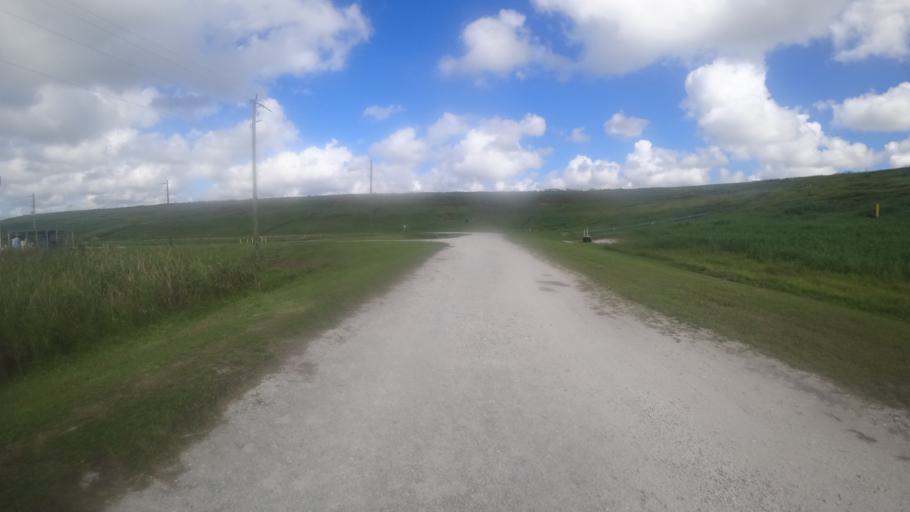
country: US
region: Florida
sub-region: Manatee County
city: Samoset
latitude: 27.4683
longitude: -82.4463
